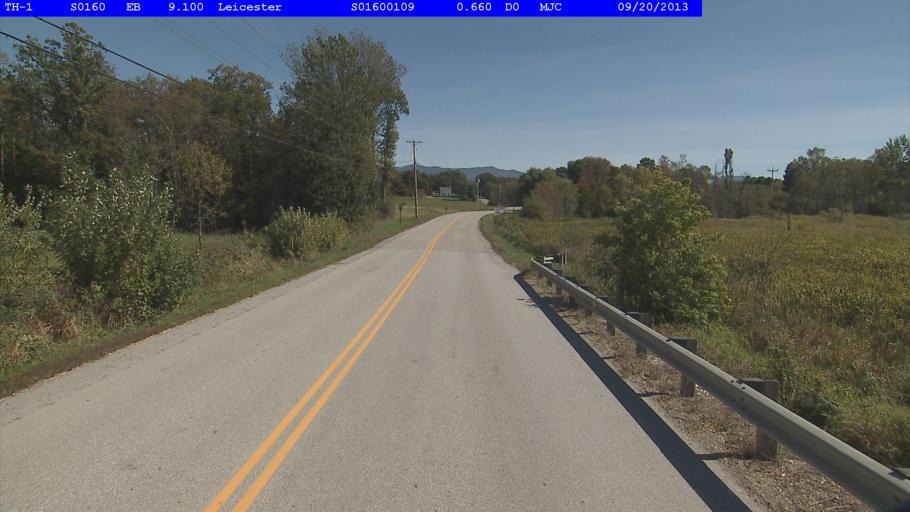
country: US
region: Vermont
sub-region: Rutland County
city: Brandon
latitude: 43.8553
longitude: -73.1468
